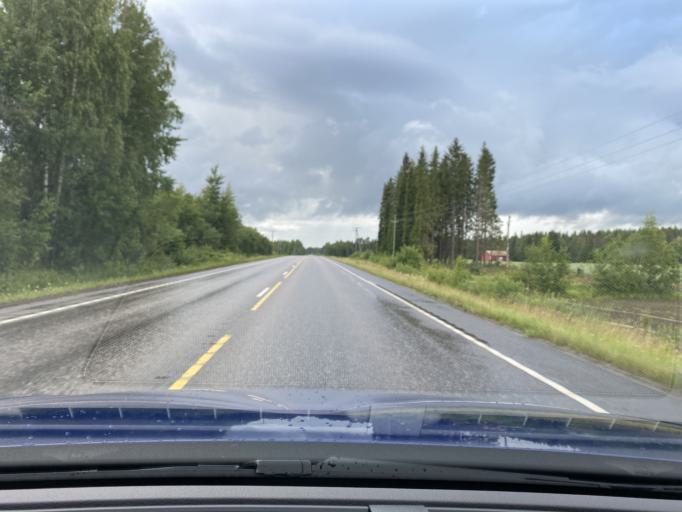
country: FI
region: Uusimaa
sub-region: Helsinki
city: Nurmijaervi
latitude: 60.5484
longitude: 24.8283
